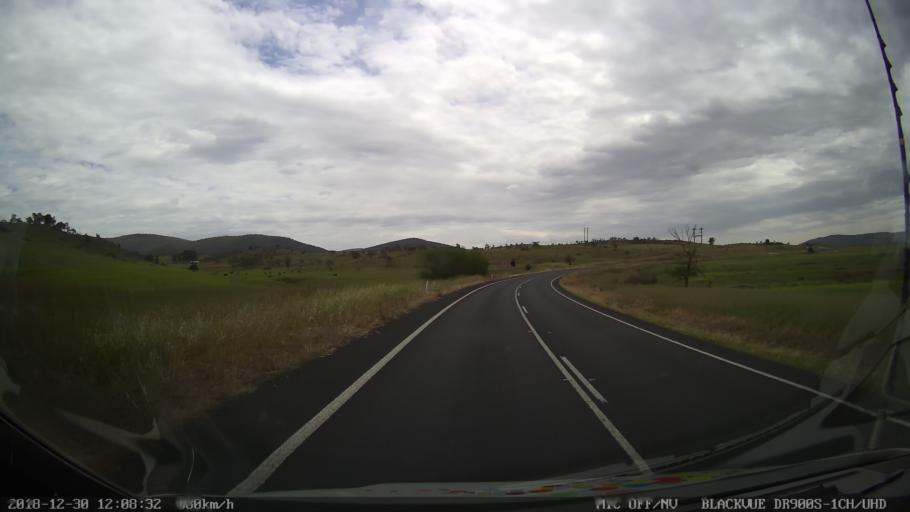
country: AU
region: New South Wales
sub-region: Snowy River
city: Jindabyne
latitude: -36.3941
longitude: 148.5941
